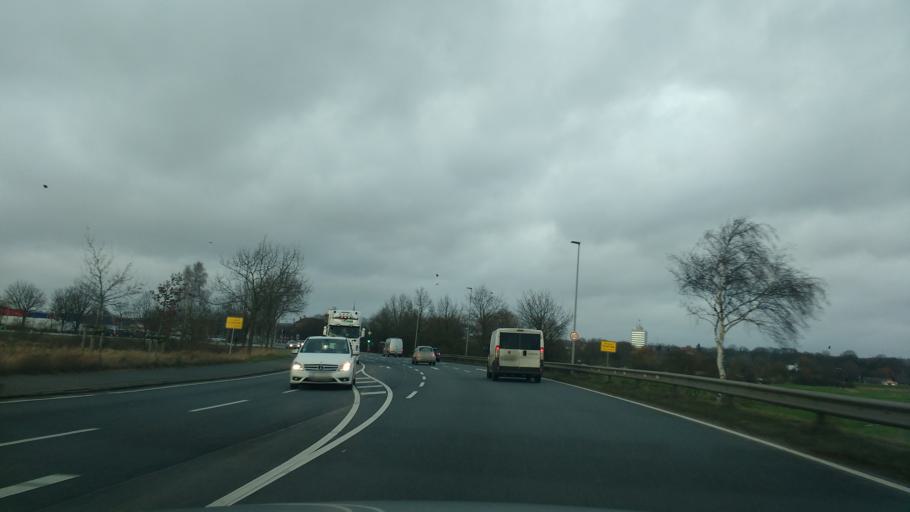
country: DE
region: Schleswig-Holstein
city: Itzehoe
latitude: 53.9116
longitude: 9.5158
